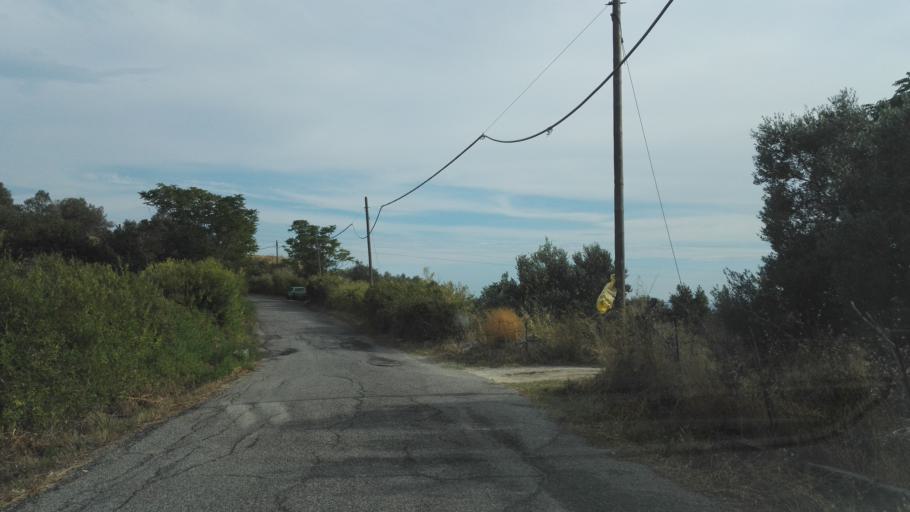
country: IT
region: Calabria
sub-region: Provincia di Reggio Calabria
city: Stignano
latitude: 38.4240
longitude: 16.4651
